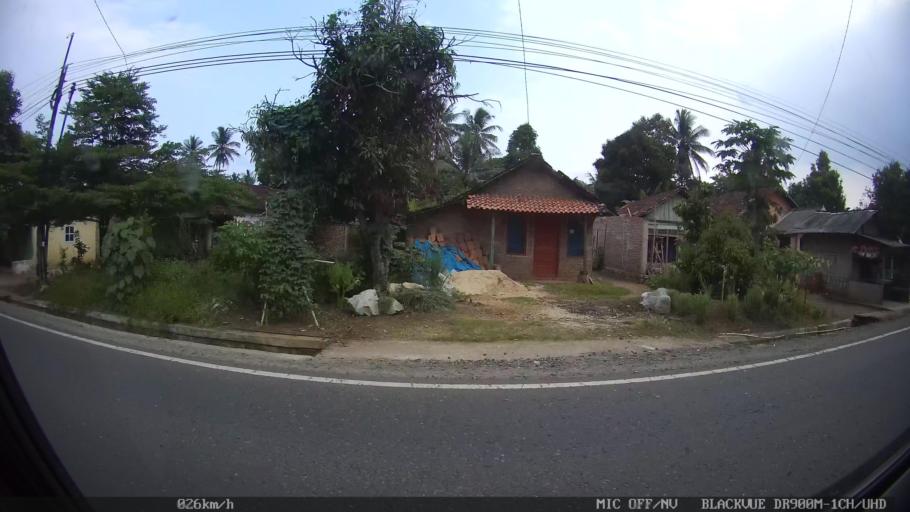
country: ID
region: Lampung
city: Gedongtataan
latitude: -5.3672
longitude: 105.1587
